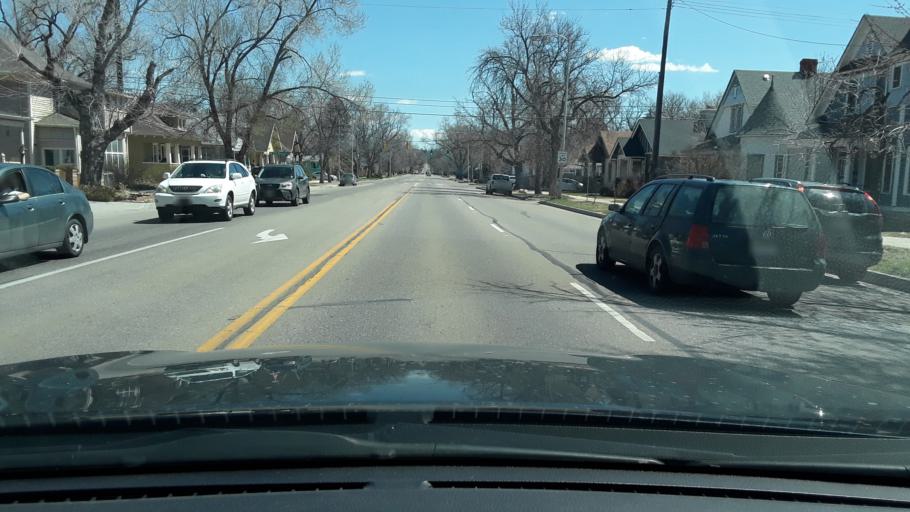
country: US
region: Colorado
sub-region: El Paso County
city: Colorado Springs
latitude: 38.8505
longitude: -104.8187
